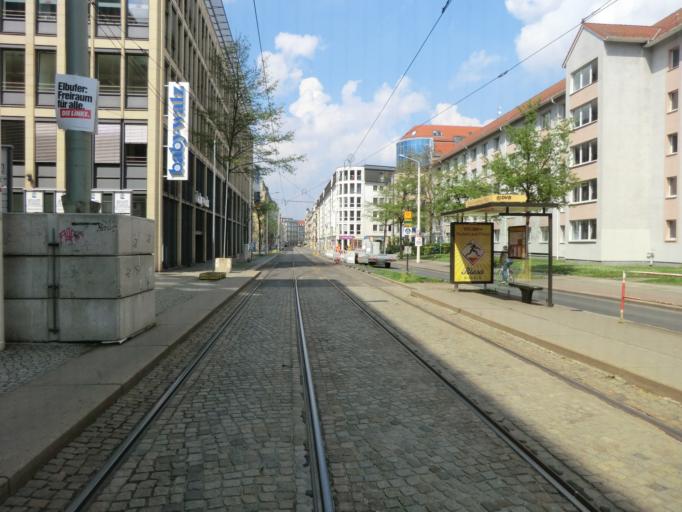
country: DE
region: Saxony
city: Dresden
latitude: 51.0607
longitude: 13.7523
